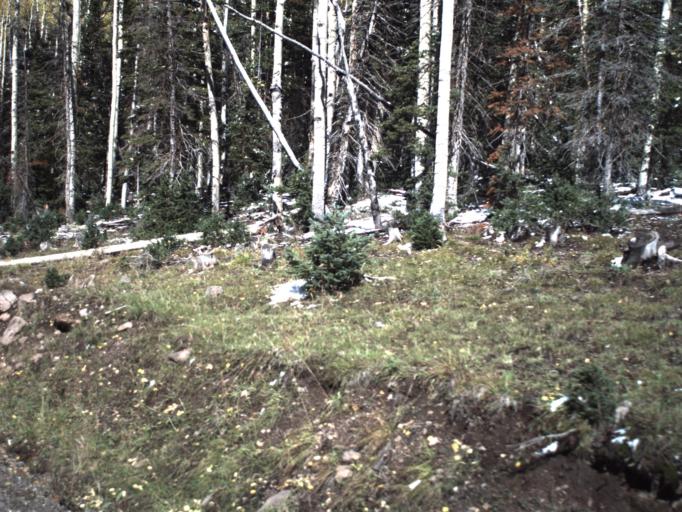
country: US
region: Utah
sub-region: Piute County
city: Junction
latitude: 38.3114
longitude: -112.3648
